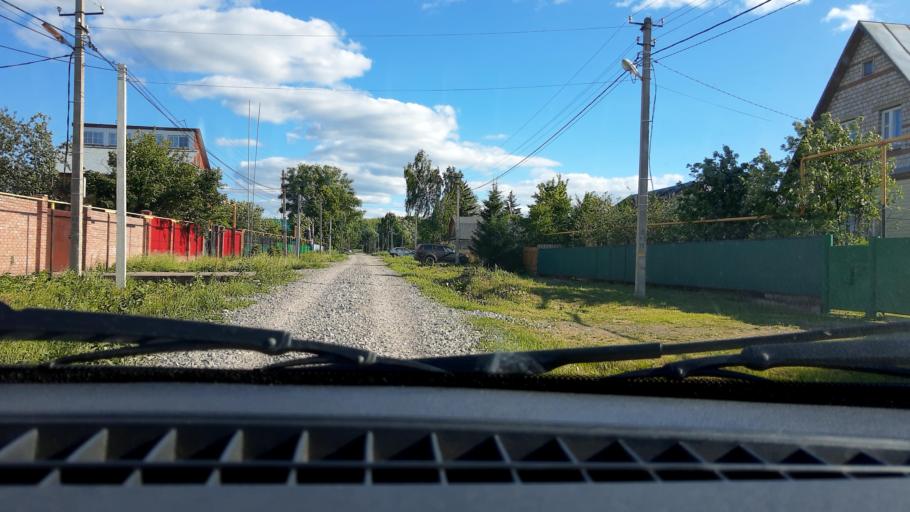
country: RU
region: Bashkortostan
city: Mikhaylovka
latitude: 54.8842
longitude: 55.8775
